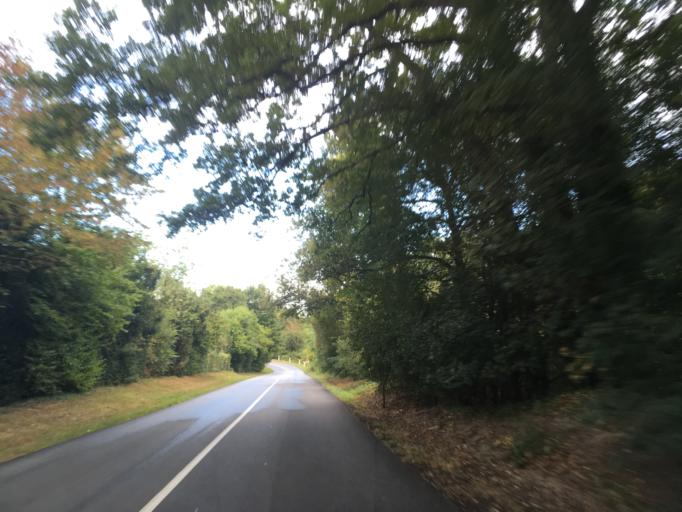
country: FR
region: Haute-Normandie
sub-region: Departement de l'Eure
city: Saint-Just
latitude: 49.1284
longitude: 1.4539
